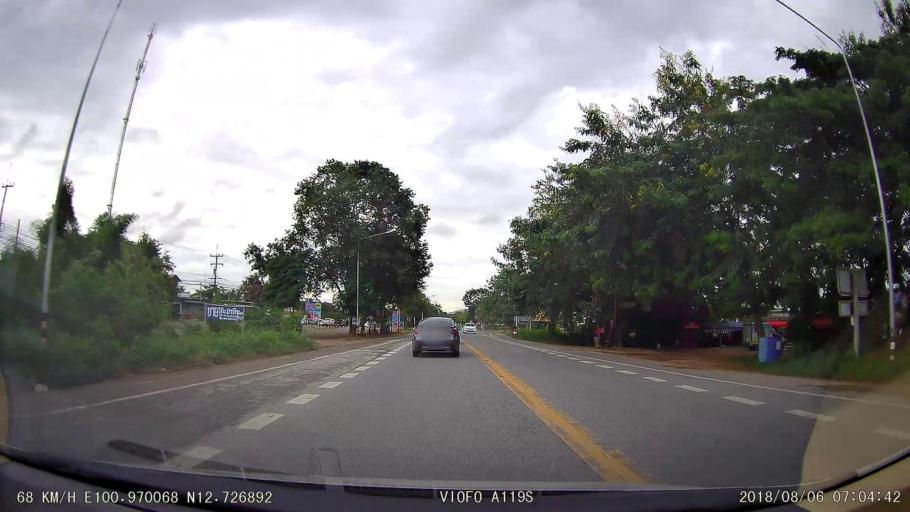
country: TH
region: Rayong
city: Ban Chang
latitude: 12.7269
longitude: 100.9702
